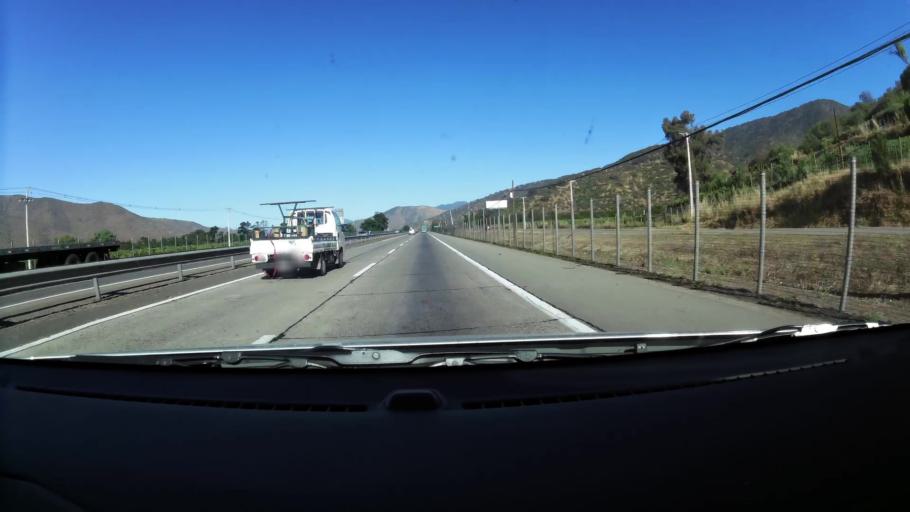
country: CL
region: Santiago Metropolitan
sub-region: Provincia de Chacabuco
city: Lampa
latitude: -33.4061
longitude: -71.0795
